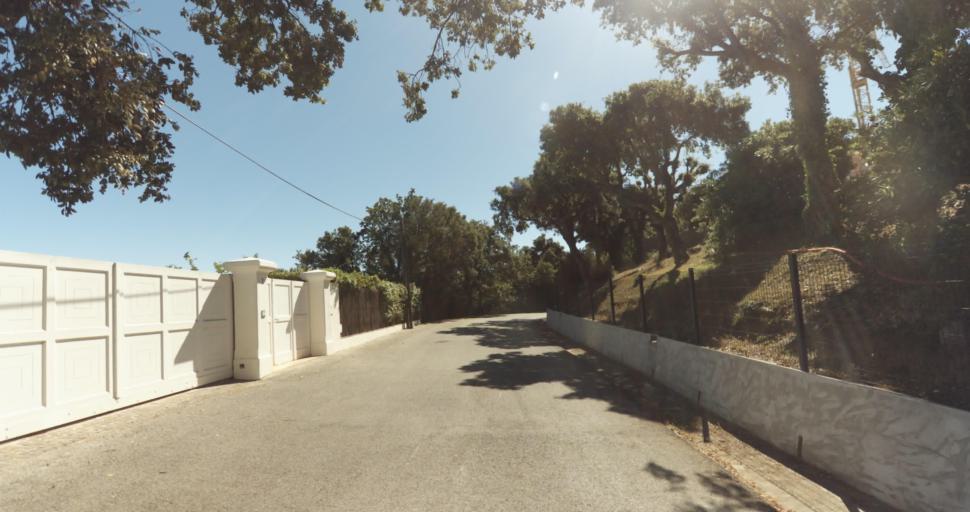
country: FR
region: Provence-Alpes-Cote d'Azur
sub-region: Departement du Var
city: Saint-Tropez
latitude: 43.2580
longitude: 6.6094
